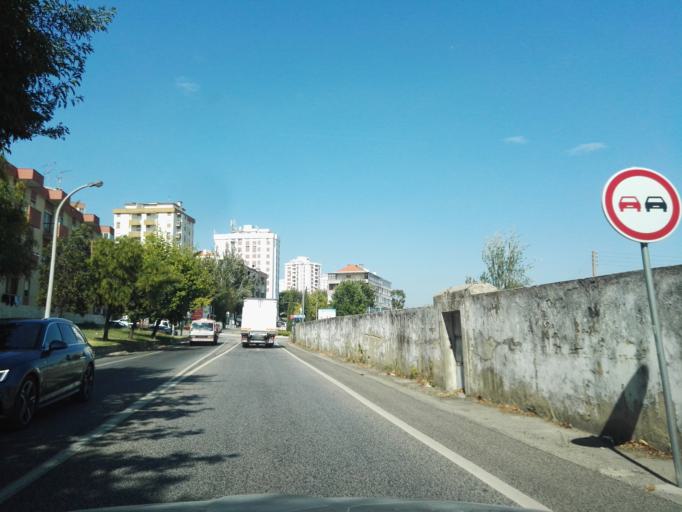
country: PT
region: Lisbon
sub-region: Vila Franca de Xira
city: Povoa de Santa Iria
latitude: 38.8543
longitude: -9.0722
